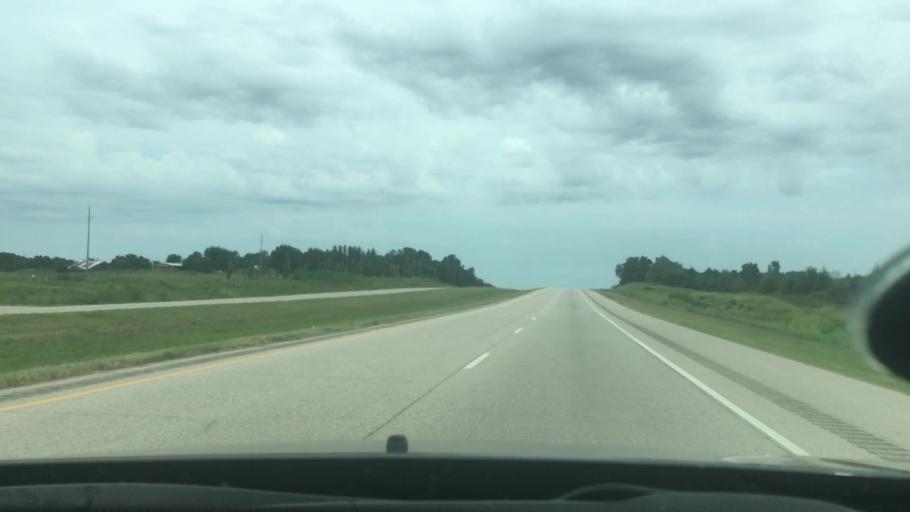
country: US
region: Oklahoma
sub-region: Pontotoc County
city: Byng
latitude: 34.9138
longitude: -96.6799
